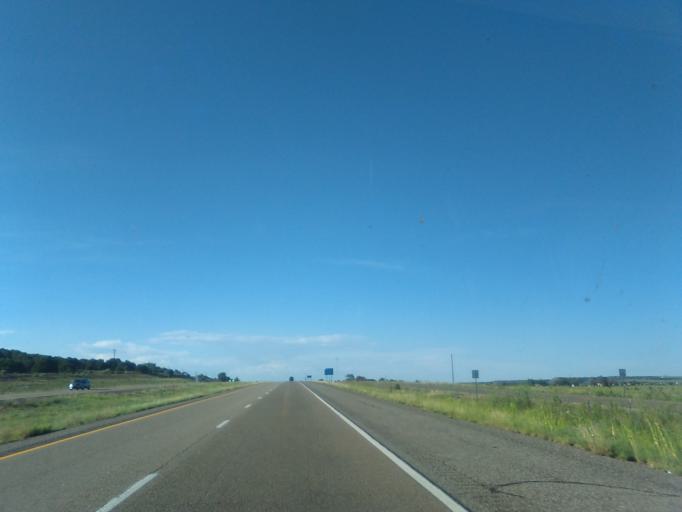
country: US
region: New Mexico
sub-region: San Miguel County
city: Las Vegas
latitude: 35.5379
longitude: -105.2291
